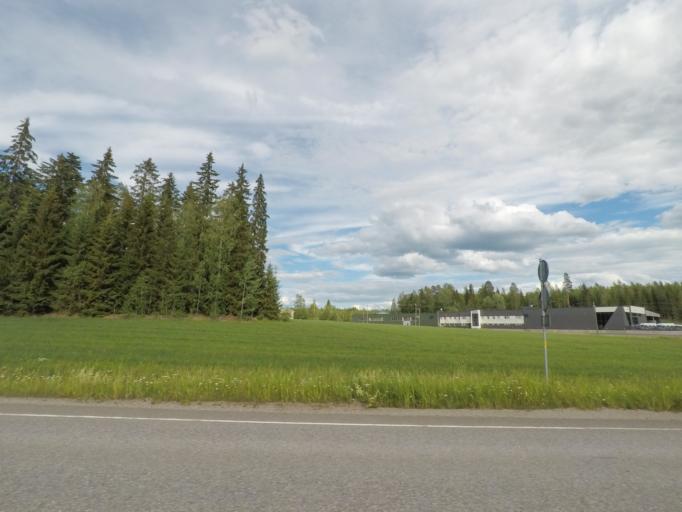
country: FI
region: Paijanne Tavastia
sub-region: Lahti
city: Hollola
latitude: 60.8655
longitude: 25.5013
